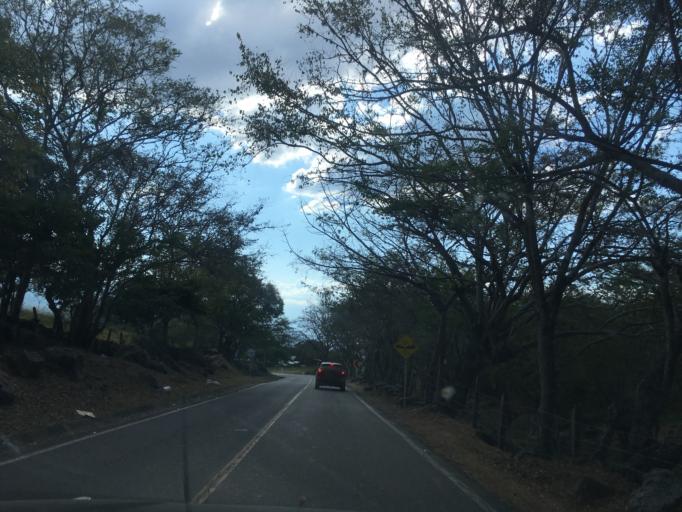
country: CO
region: Santander
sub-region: San Gil
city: San Gil
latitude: 6.5677
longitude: -73.1451
